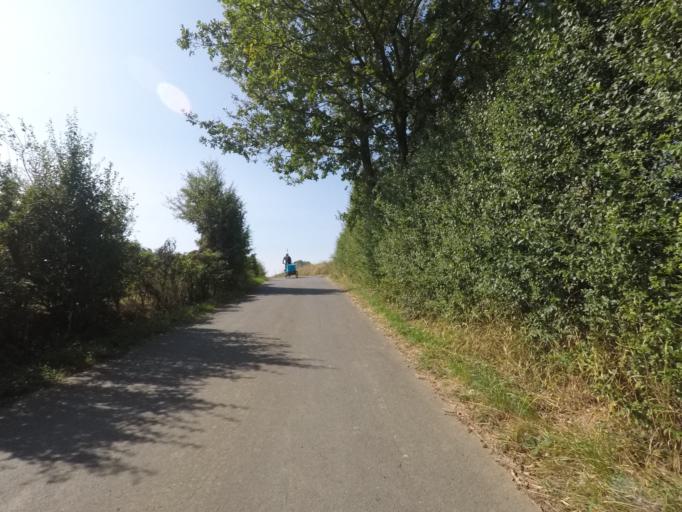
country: LU
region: Luxembourg
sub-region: Canton de Capellen
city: Mamer
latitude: 49.6475
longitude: 6.0206
